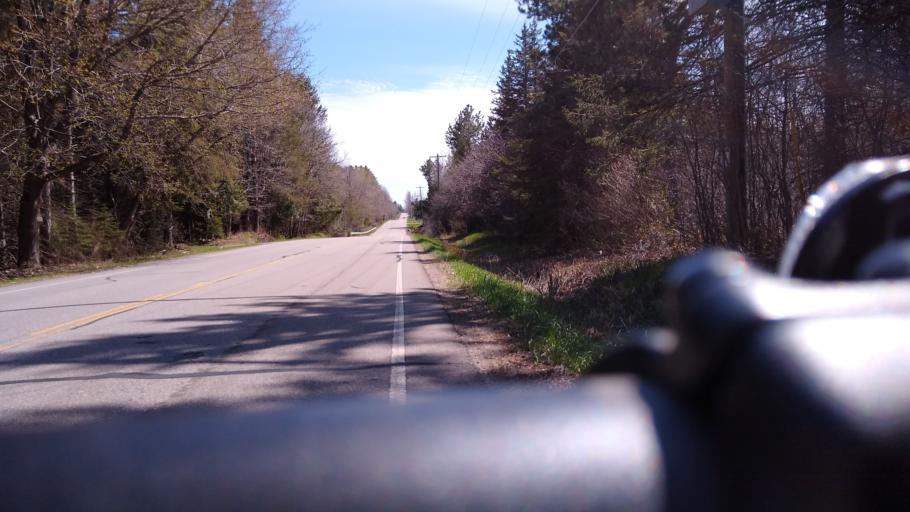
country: US
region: Michigan
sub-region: Delta County
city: Escanaba
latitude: 45.7305
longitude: -87.2025
